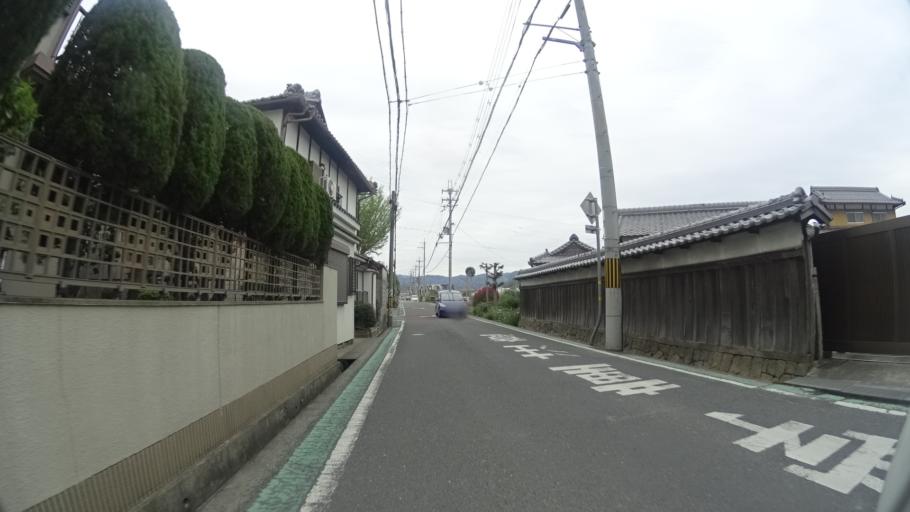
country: JP
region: Kyoto
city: Kameoka
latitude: 35.0280
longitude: 135.5596
